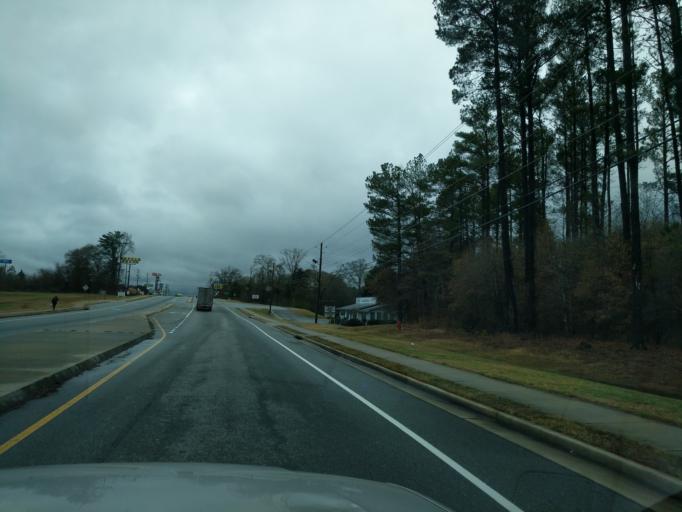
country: US
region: Georgia
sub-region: Franklin County
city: Lavonia
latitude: 34.4436
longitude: -83.1145
